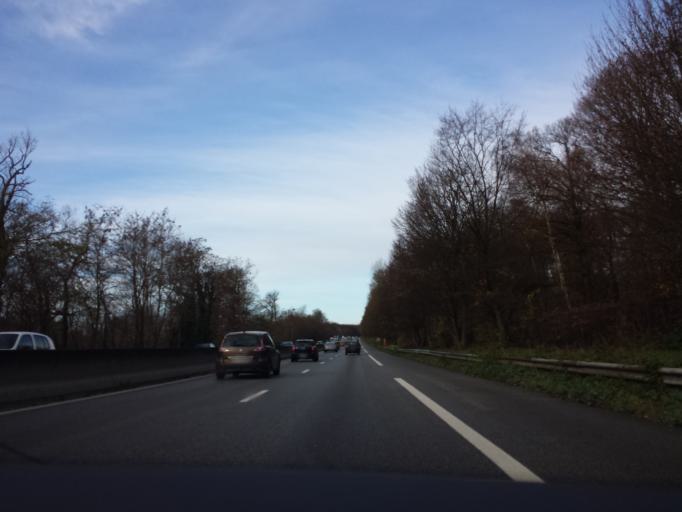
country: FR
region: Ile-de-France
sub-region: Departement des Yvelines
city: Saint-Nom-la-Breteche
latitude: 48.8623
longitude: 2.0438
